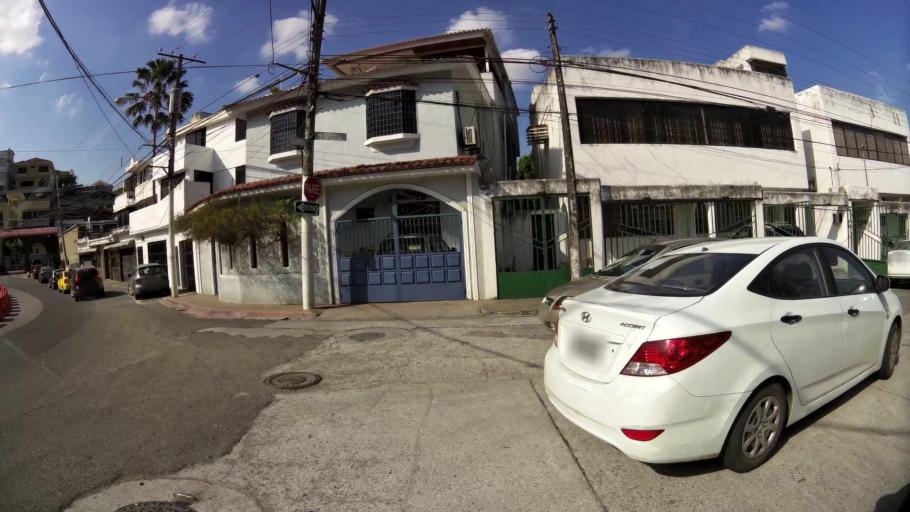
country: EC
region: Guayas
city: Santa Lucia
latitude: -2.1579
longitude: -79.9464
